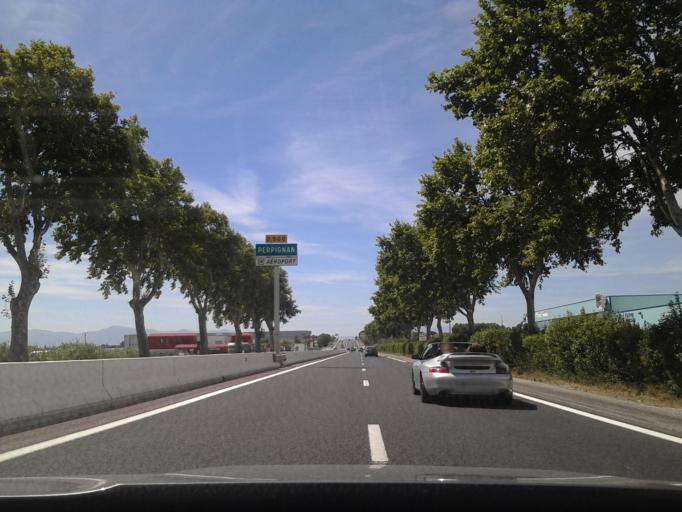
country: FR
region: Languedoc-Roussillon
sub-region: Departement des Pyrenees-Orientales
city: Pia
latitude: 42.7593
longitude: 2.8973
